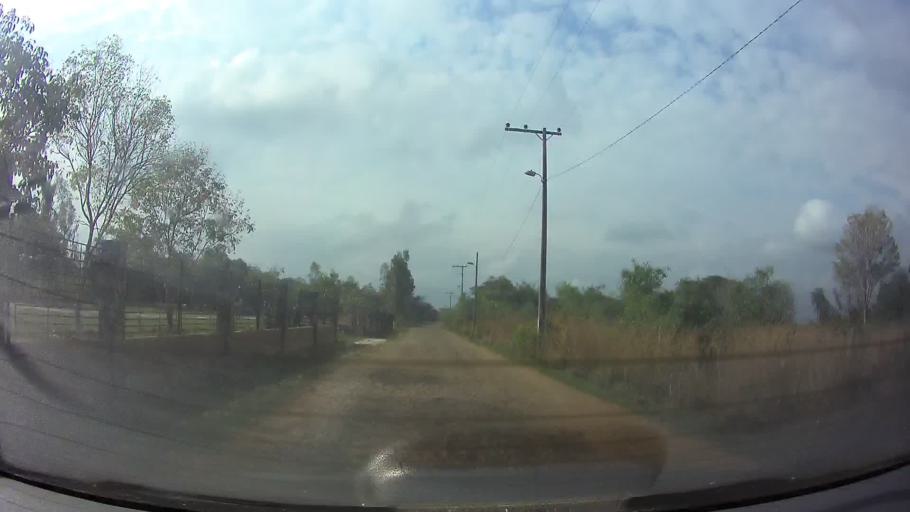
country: PY
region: Cordillera
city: Arroyos y Esteros
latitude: -24.9958
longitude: -57.1940
